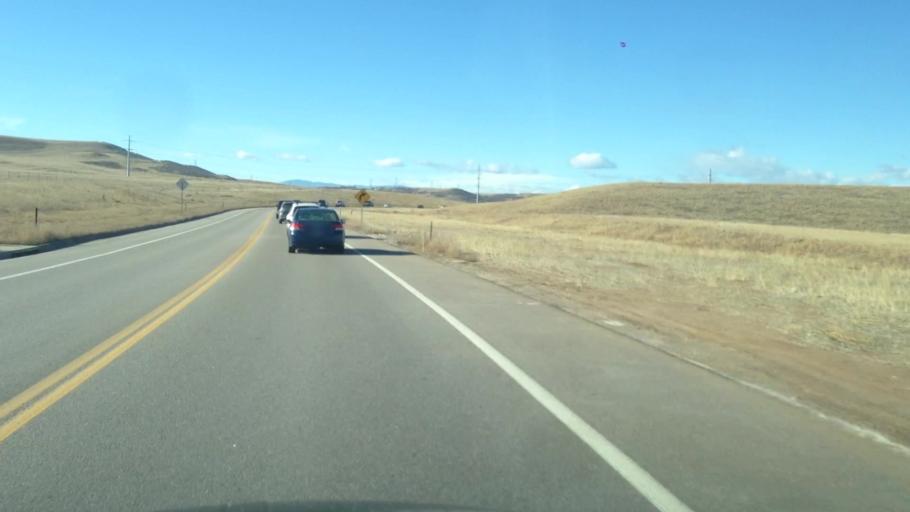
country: US
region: Colorado
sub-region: Douglas County
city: Meridian
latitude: 39.5209
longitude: -104.8419
